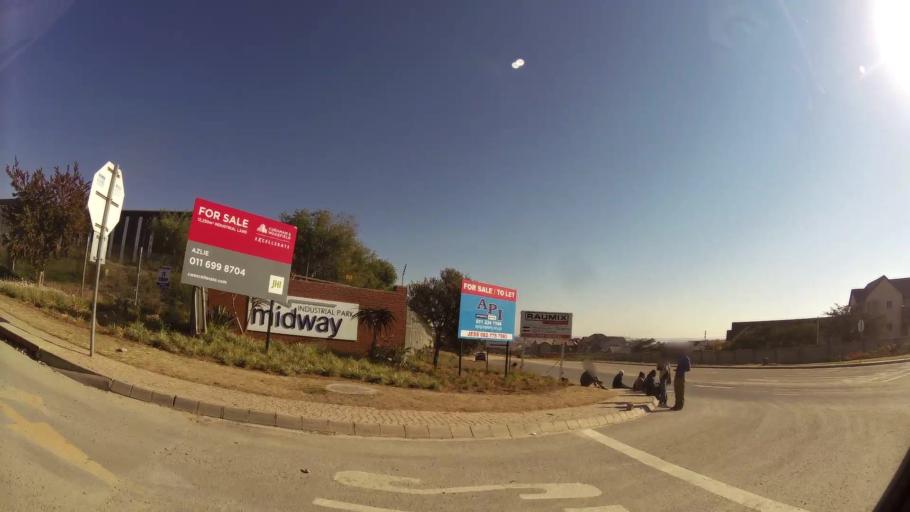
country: ZA
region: Gauteng
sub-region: City of Johannesburg Metropolitan Municipality
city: Midrand
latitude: -25.9182
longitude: 28.1273
